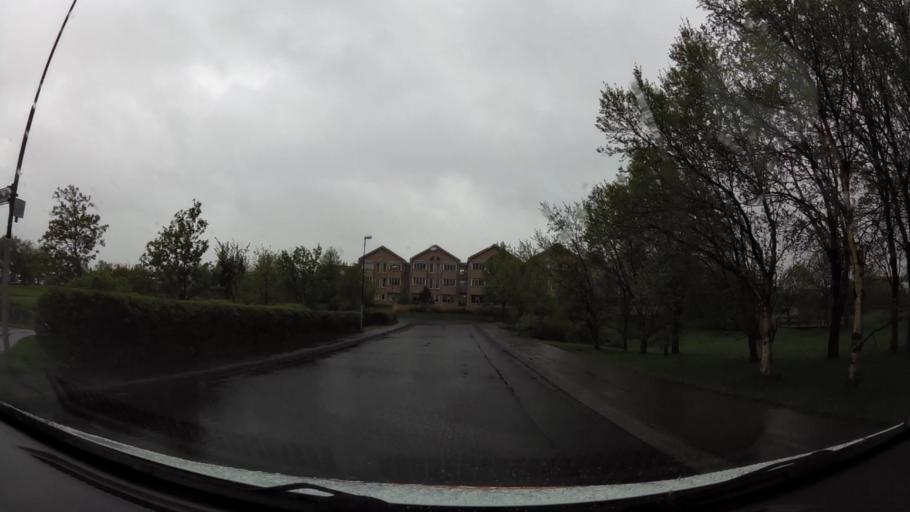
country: IS
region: Capital Region
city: Reykjavik
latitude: 64.0968
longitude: -21.8432
